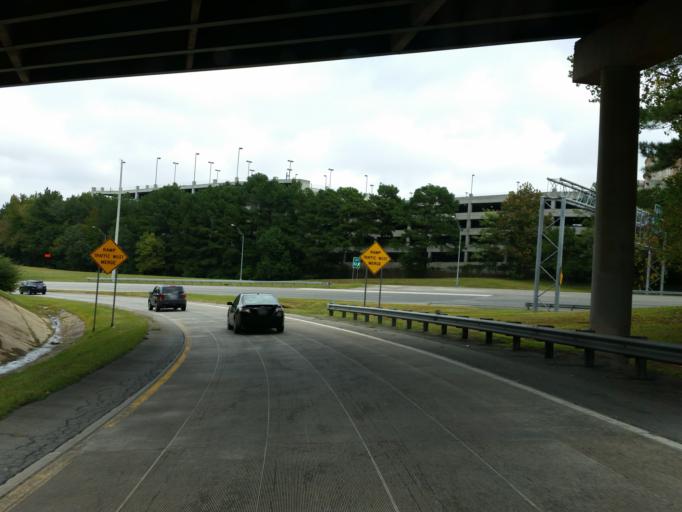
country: US
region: Georgia
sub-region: Fulton County
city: Sandy Springs
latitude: 33.9097
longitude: -84.3575
